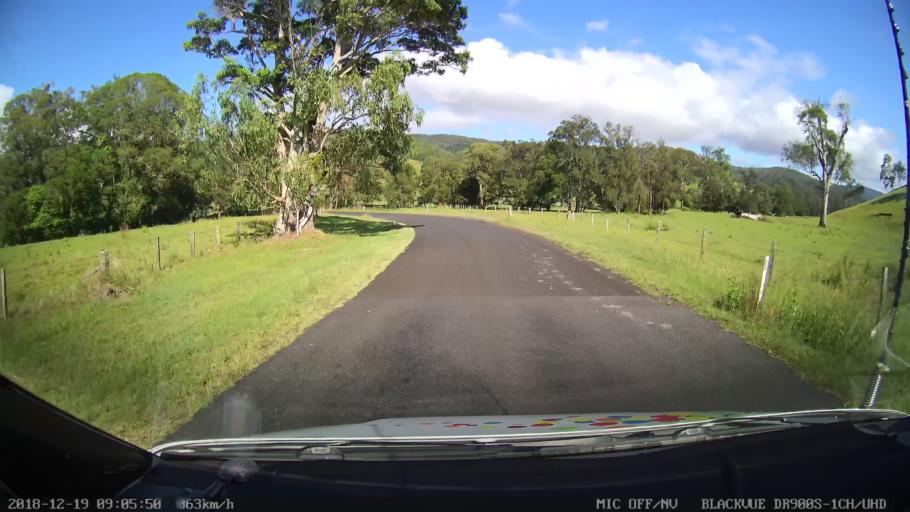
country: AU
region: New South Wales
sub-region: Kyogle
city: Kyogle
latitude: -28.4641
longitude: 152.9383
